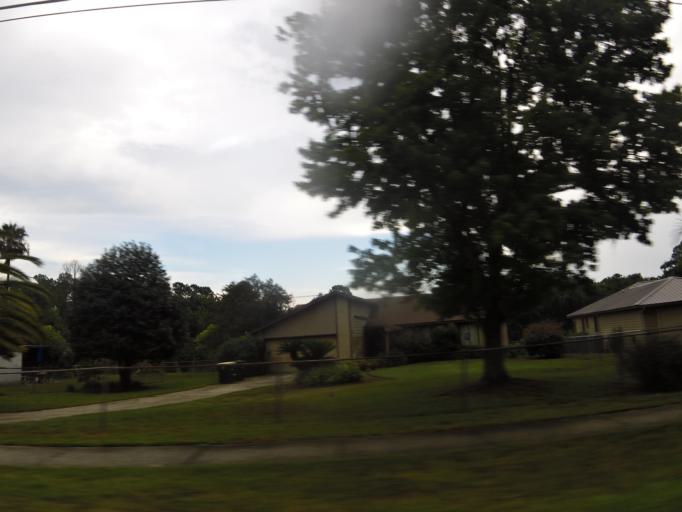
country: US
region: Florida
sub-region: Duval County
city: Jacksonville
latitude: 30.3059
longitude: -81.5413
